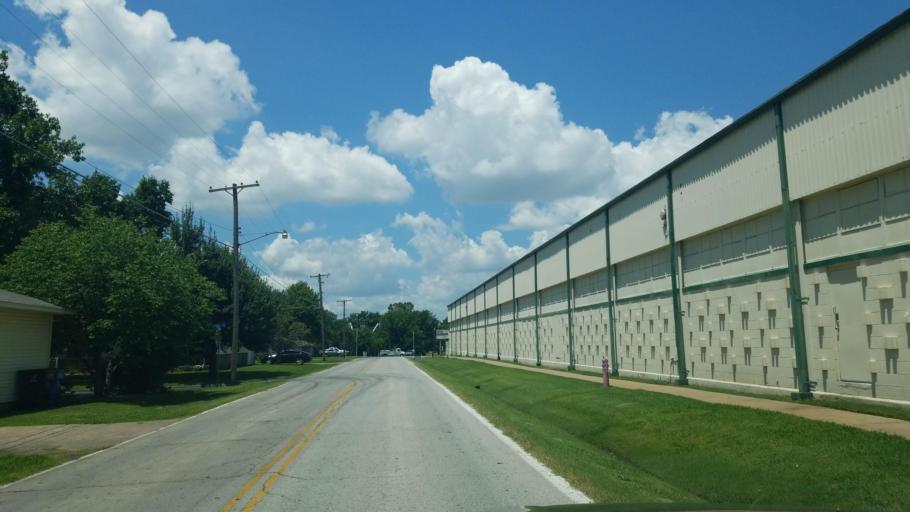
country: US
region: Oklahoma
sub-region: Tulsa County
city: Broken Arrow
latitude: 36.0502
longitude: -95.7812
